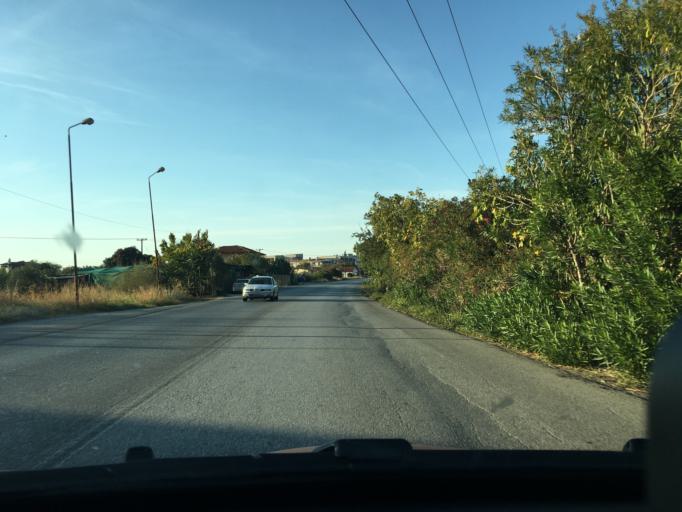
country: GR
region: Central Macedonia
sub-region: Nomos Chalkidikis
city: Nea Potidhaia
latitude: 40.2031
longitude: 23.3253
